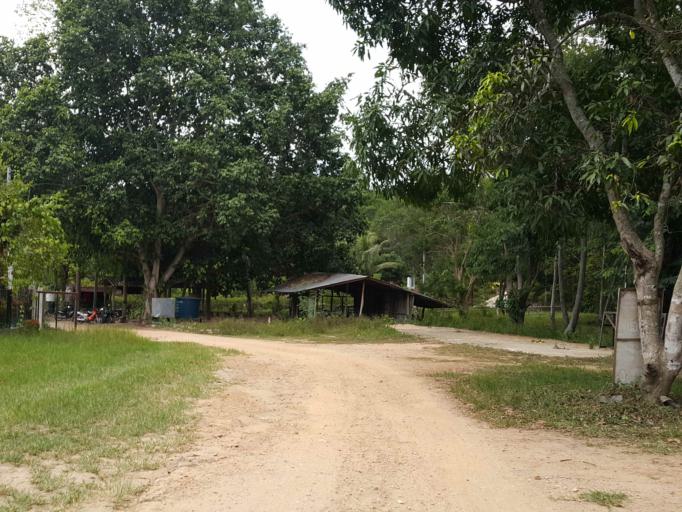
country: TH
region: Chiang Mai
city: Hang Dong
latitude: 18.7625
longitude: 98.9058
